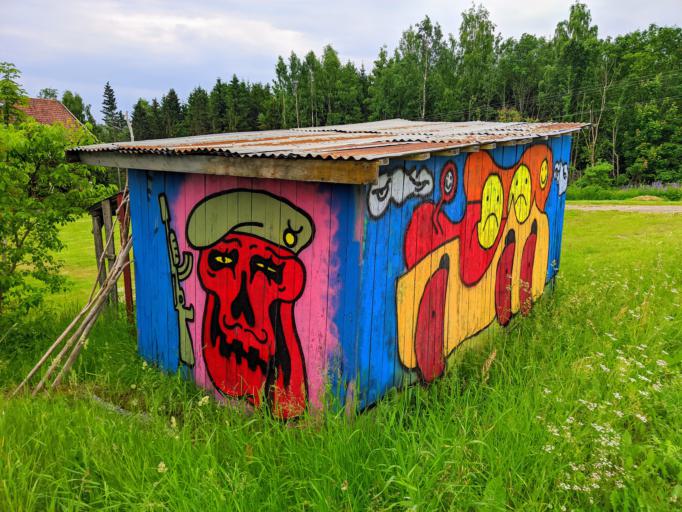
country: NO
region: Akershus
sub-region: Hurdal
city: Hurdal
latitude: 60.4884
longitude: 11.1506
